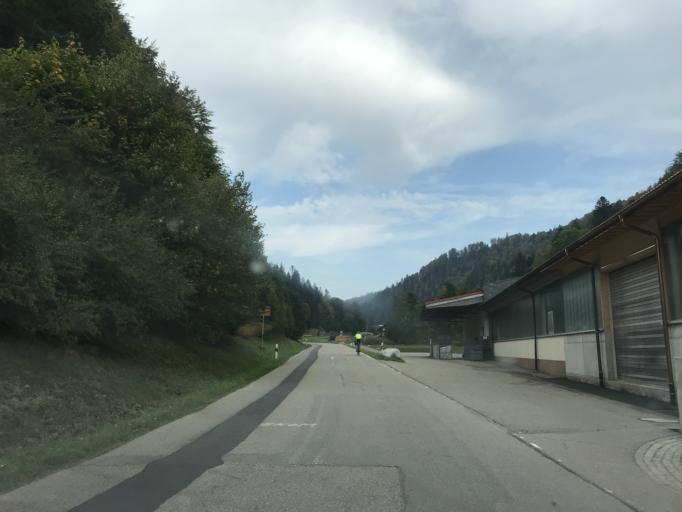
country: DE
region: Baden-Wuerttemberg
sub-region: Freiburg Region
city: Herrischried
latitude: 47.6975
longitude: 7.9821
